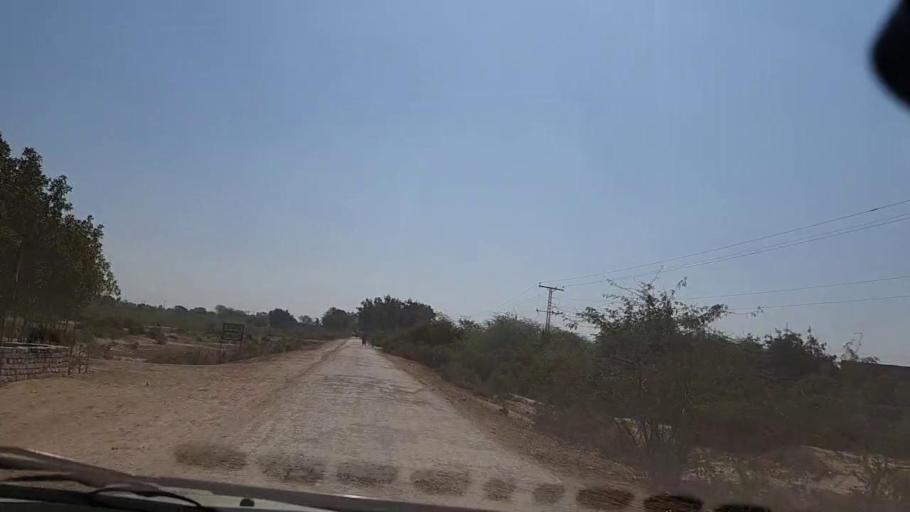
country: PK
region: Sindh
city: Mirpur Khas
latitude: 25.4765
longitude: 69.0487
